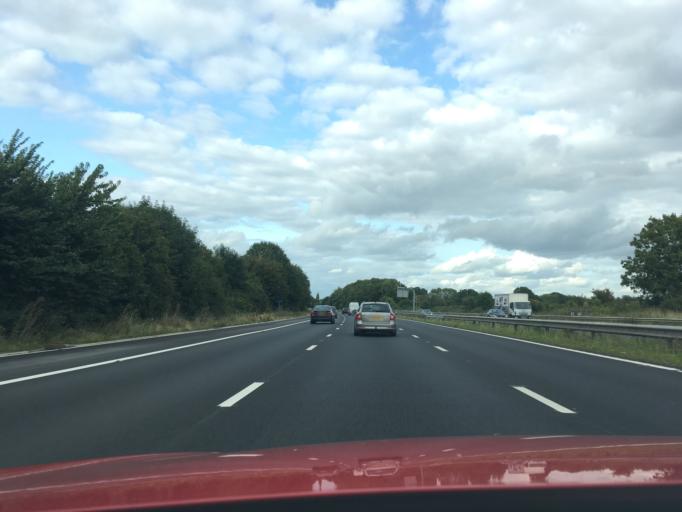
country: GB
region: England
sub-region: Gloucestershire
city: Barnwood
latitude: 51.8418
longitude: -2.1914
